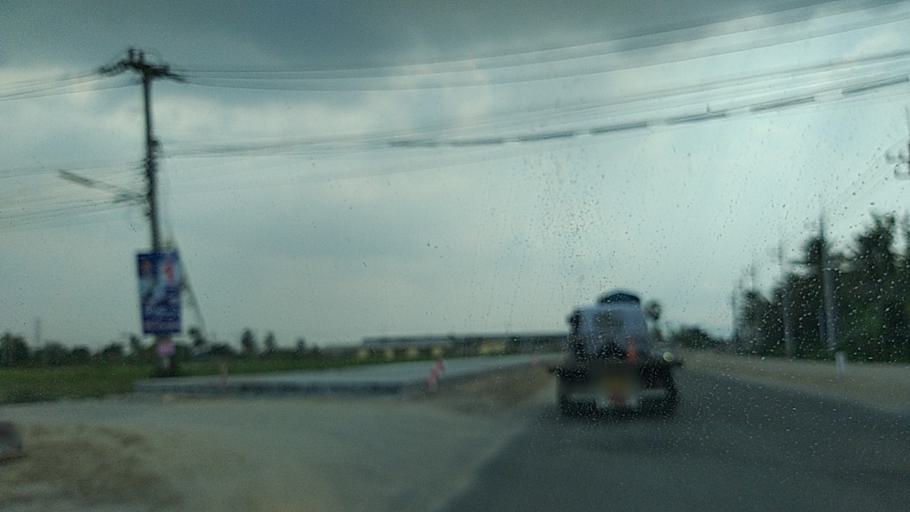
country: TH
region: Chon Buri
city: Ban Bueng
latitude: 13.3120
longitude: 101.1840
